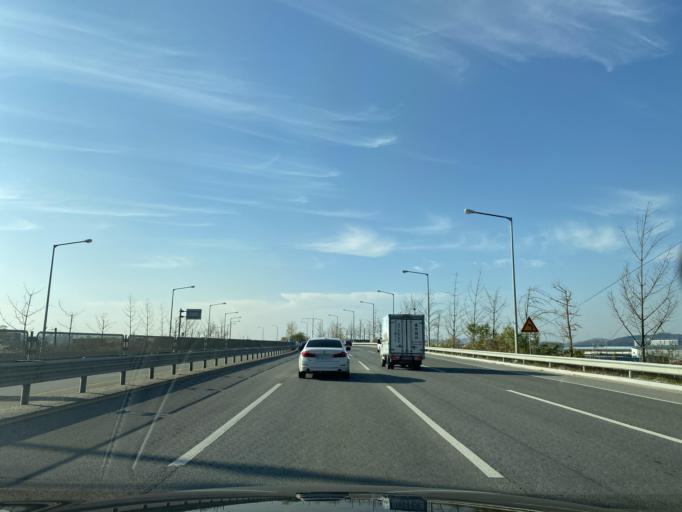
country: KR
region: Chungcheongnam-do
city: Asan
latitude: 36.7789
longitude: 127.0682
